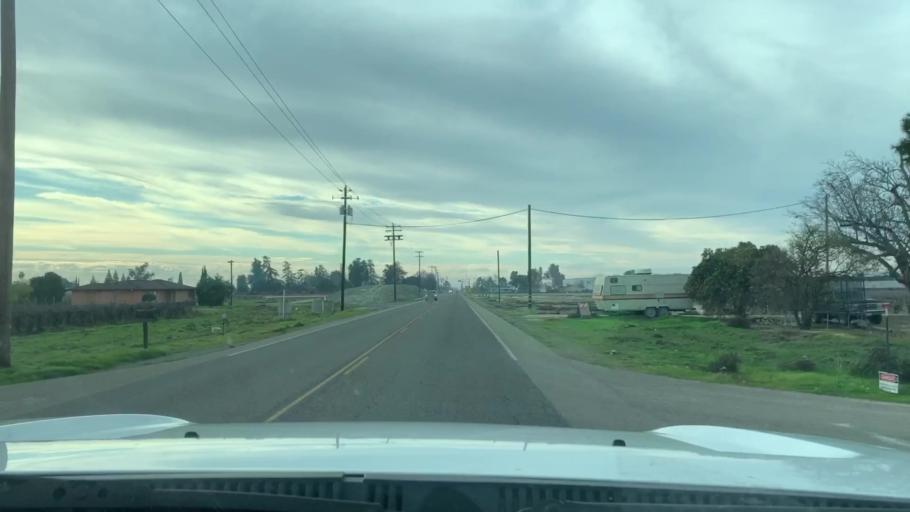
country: US
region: California
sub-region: Fresno County
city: Easton
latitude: 36.6054
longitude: -119.7460
